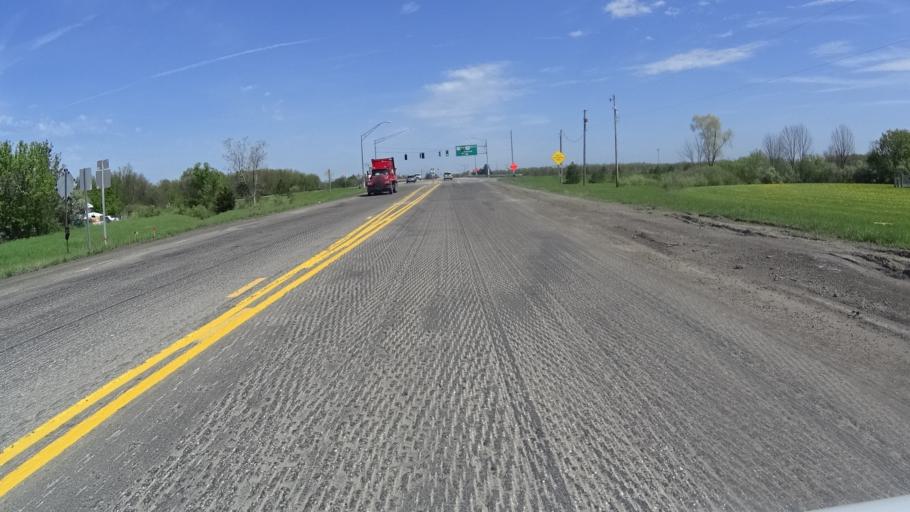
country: US
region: Ohio
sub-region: Lorain County
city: Elyria
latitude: 41.3158
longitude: -82.1176
